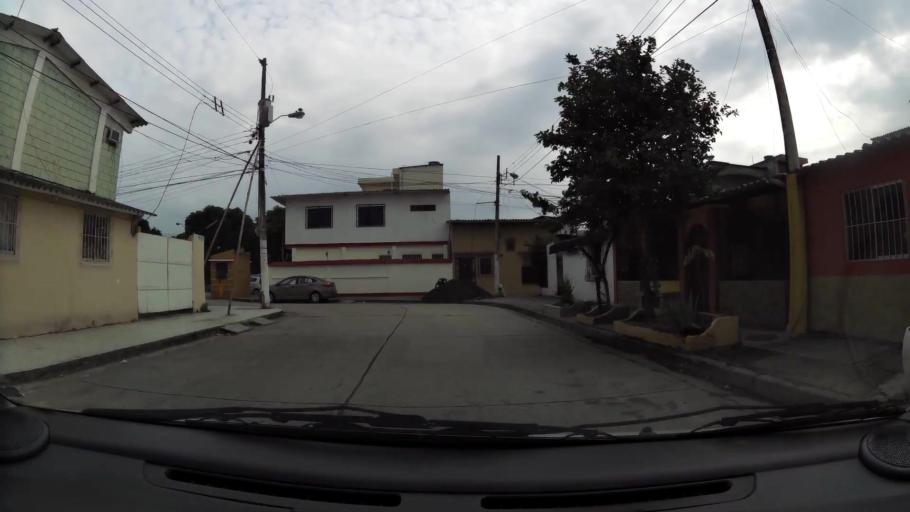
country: EC
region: Guayas
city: Eloy Alfaro
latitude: -2.1360
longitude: -79.8877
